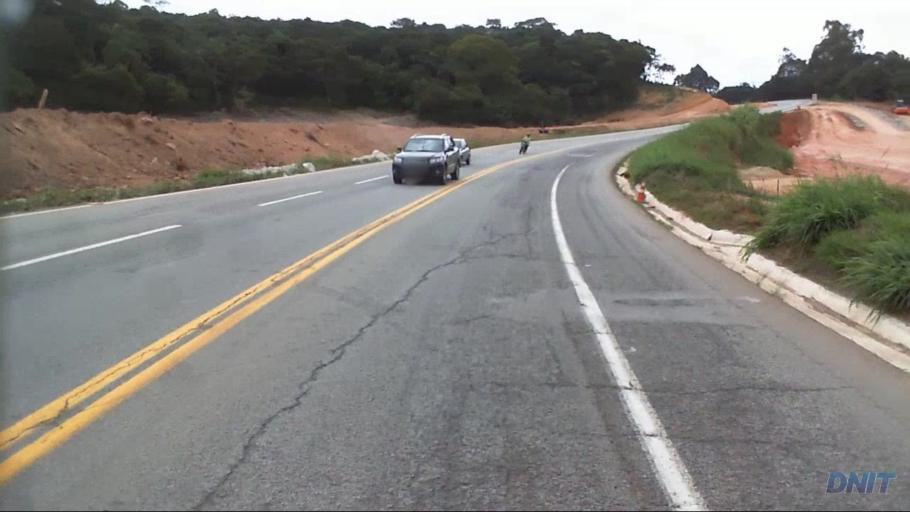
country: BR
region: Minas Gerais
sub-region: Caete
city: Caete
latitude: -19.7469
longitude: -43.5478
